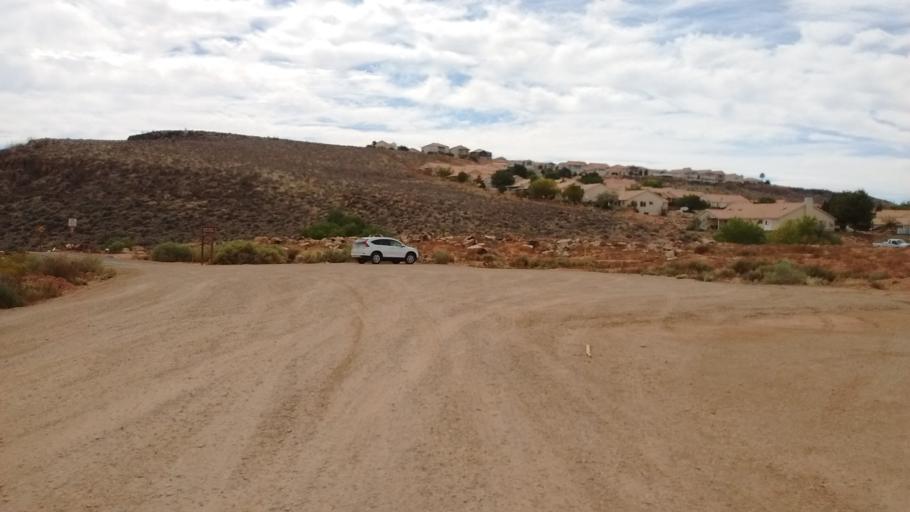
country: US
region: Utah
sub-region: Washington County
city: Washington
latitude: 37.1303
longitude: -113.4853
